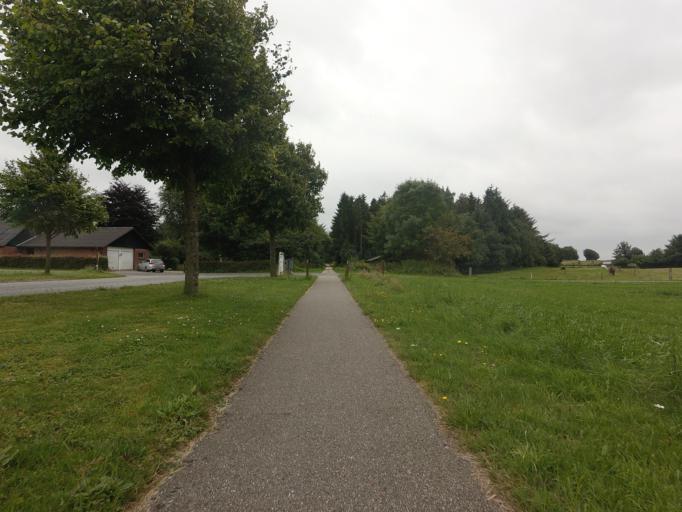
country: DK
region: Central Jutland
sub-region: Horsens Kommune
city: Braedstrup
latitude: 55.9815
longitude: 9.5957
